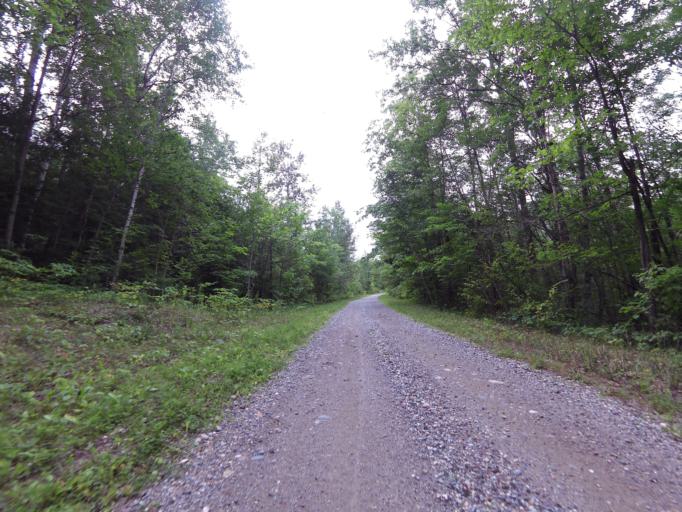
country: CA
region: Ontario
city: Perth
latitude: 44.7995
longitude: -76.6407
